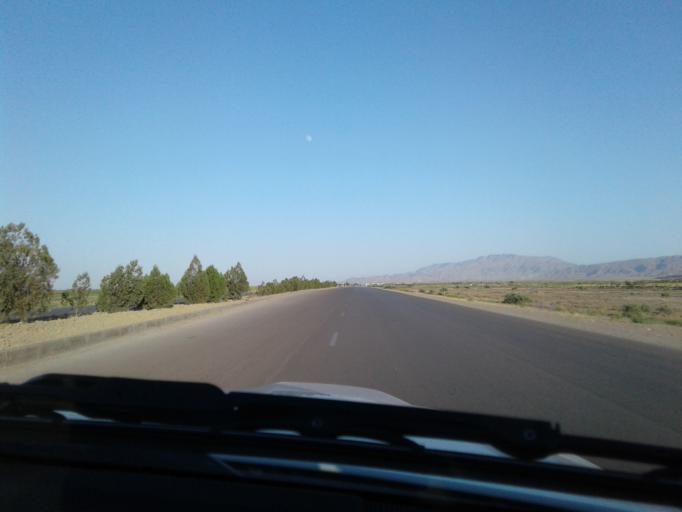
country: TM
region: Ahal
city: Baharly
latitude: 38.3627
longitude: 57.5293
